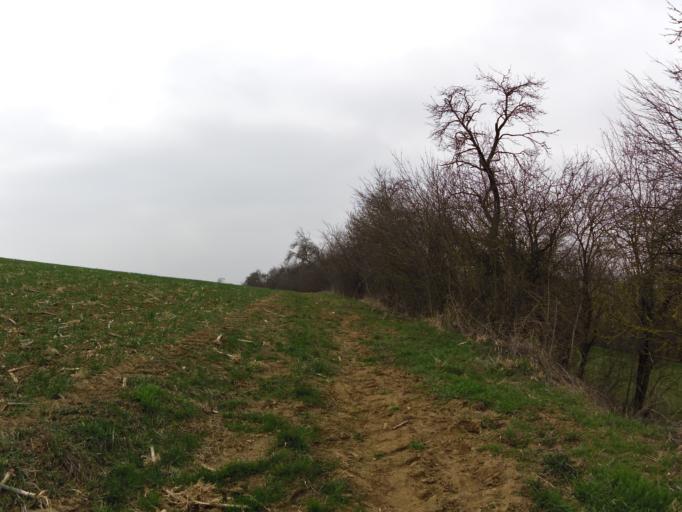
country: DE
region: Bavaria
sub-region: Regierungsbezirk Unterfranken
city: Rottendorf
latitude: 49.8213
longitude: 10.0367
